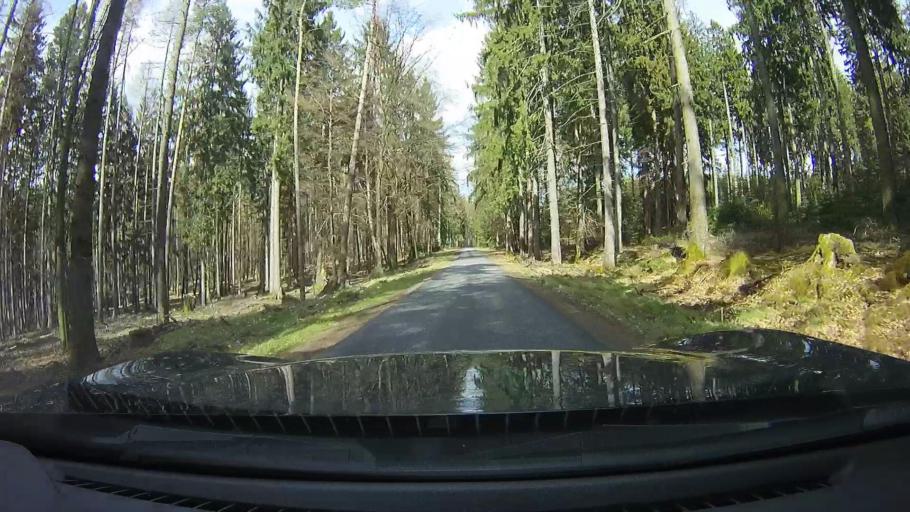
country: DE
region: Hesse
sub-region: Regierungsbezirk Darmstadt
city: Hesseneck
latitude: 49.6188
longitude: 9.0770
